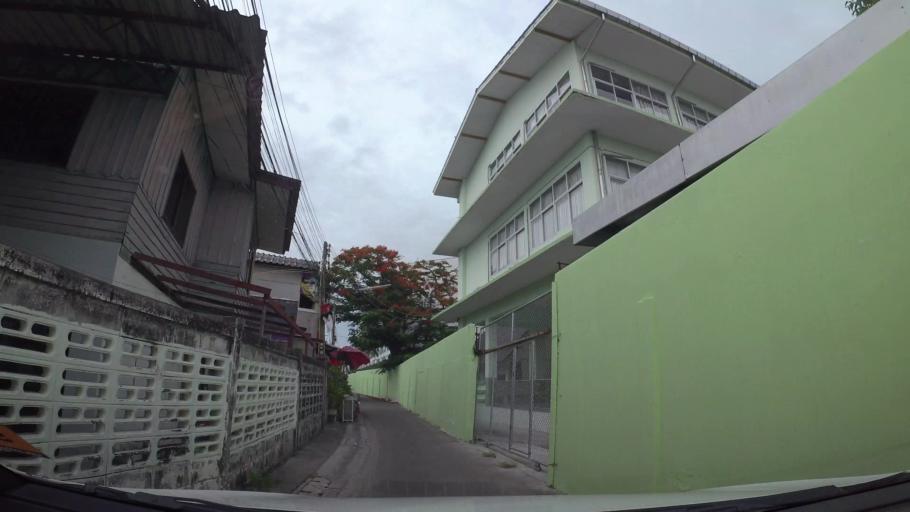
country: TH
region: Rayong
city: Rayong
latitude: 12.6636
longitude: 101.2704
